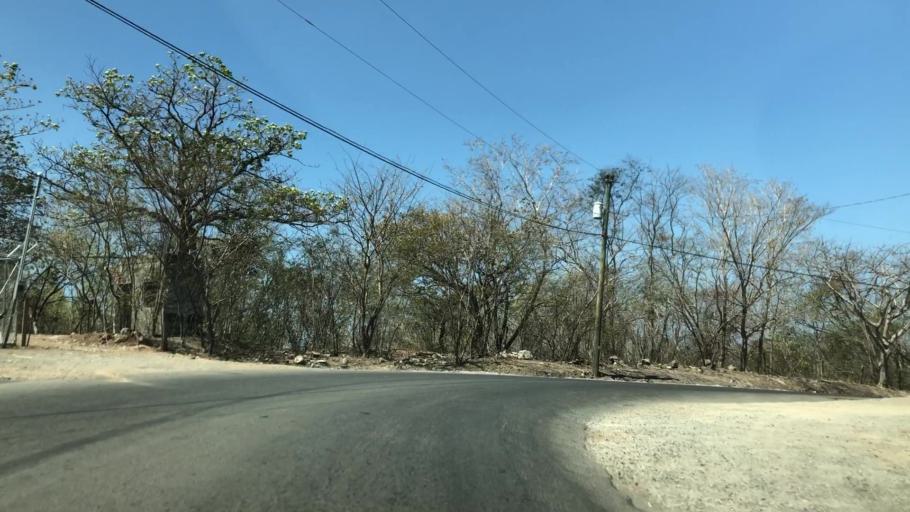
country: CR
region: Guanacaste
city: Belen
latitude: 10.3482
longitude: -85.8229
